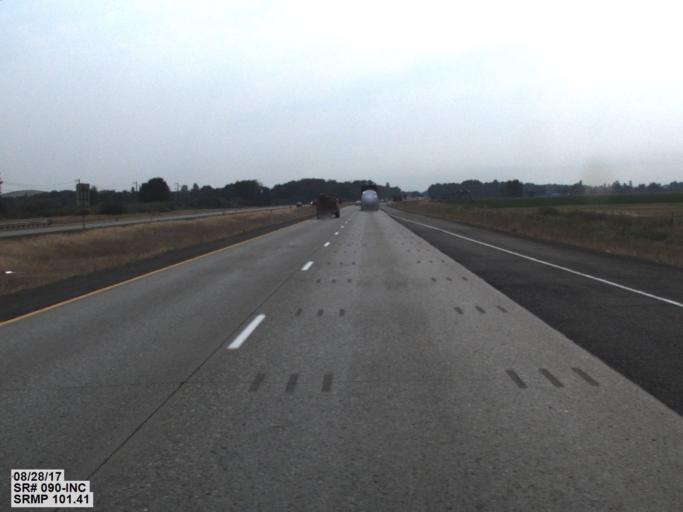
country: US
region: Washington
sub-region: Kittitas County
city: Ellensburg
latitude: 47.0519
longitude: -120.6598
